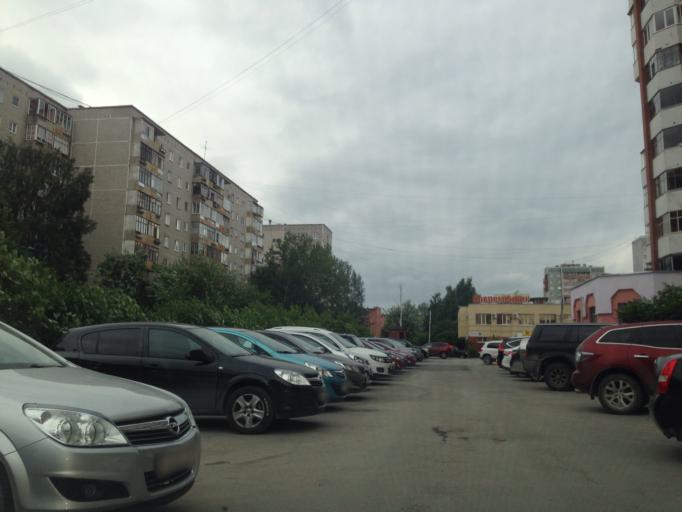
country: RU
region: Sverdlovsk
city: Yekaterinburg
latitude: 56.8305
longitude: 60.6859
